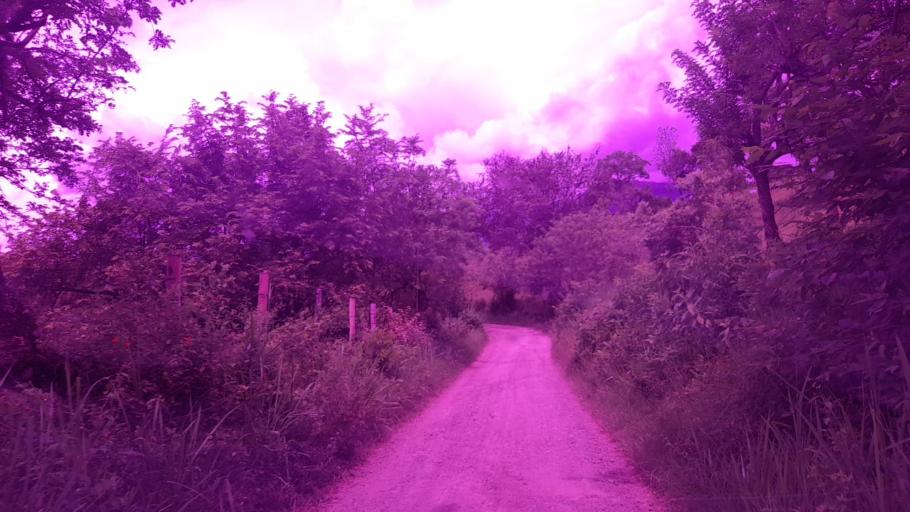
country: CO
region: Valle del Cauca
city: Andalucia
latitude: 4.1719
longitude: -76.1029
